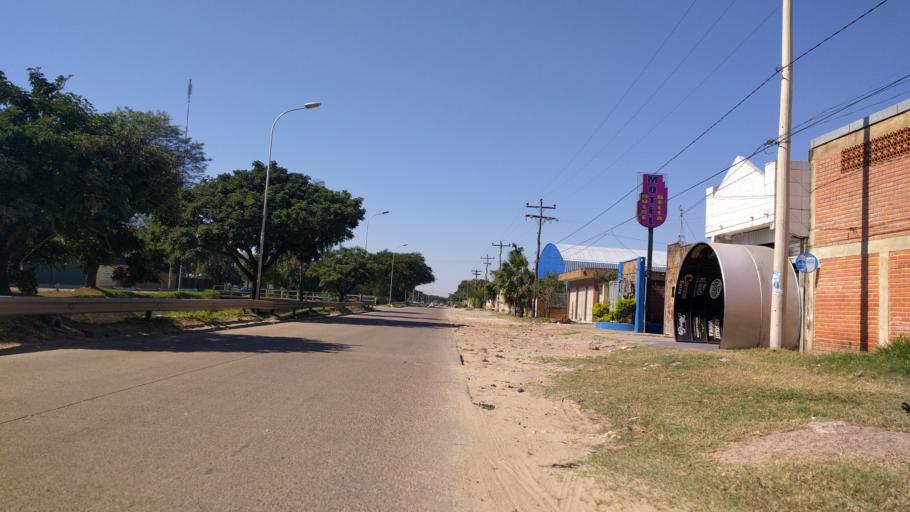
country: BO
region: Santa Cruz
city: Santa Cruz de la Sierra
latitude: -17.8194
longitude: -63.2237
